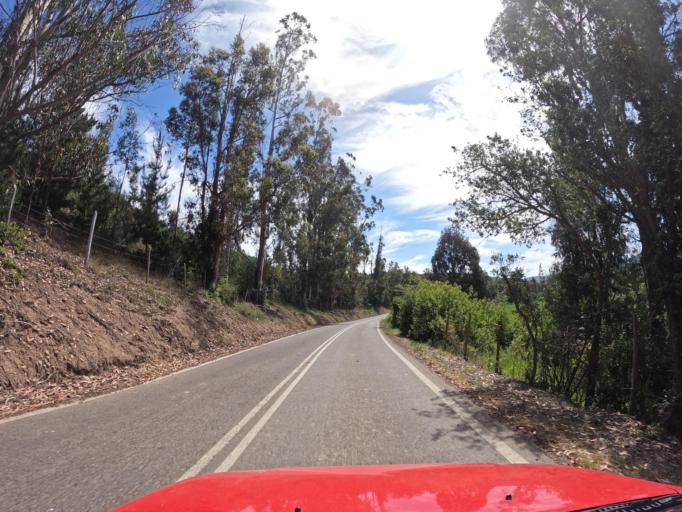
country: CL
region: Maule
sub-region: Provincia de Talca
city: Talca
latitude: -35.0059
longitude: -71.9802
